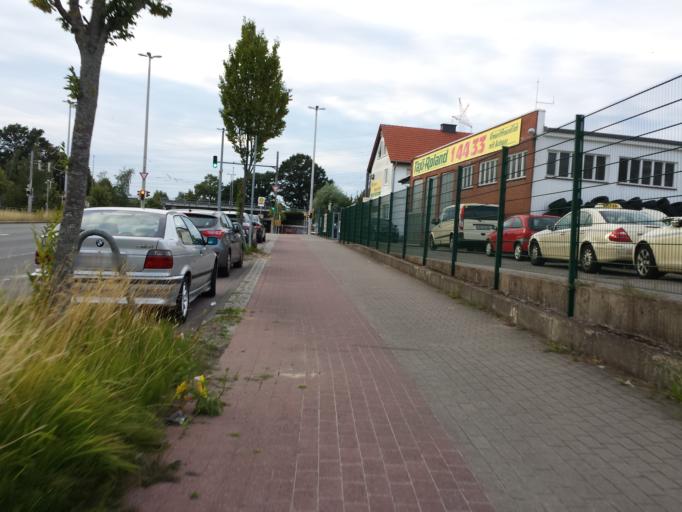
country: DE
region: Bremen
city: Bremen
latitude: 53.0613
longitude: 8.7746
